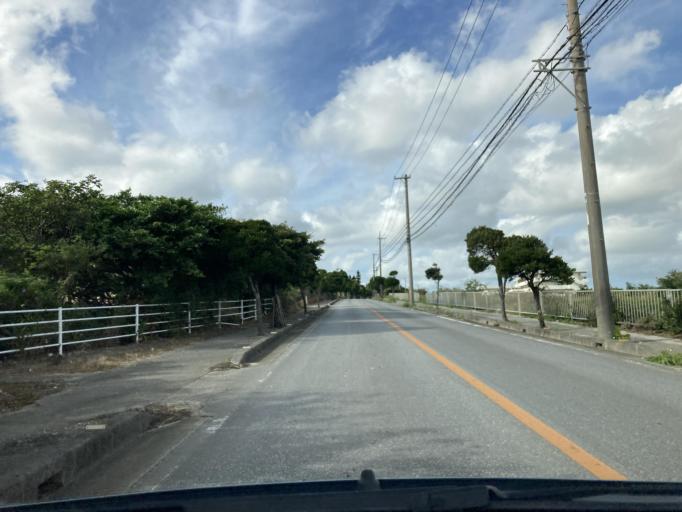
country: JP
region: Okinawa
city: Itoman
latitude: 26.1132
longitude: 127.7185
